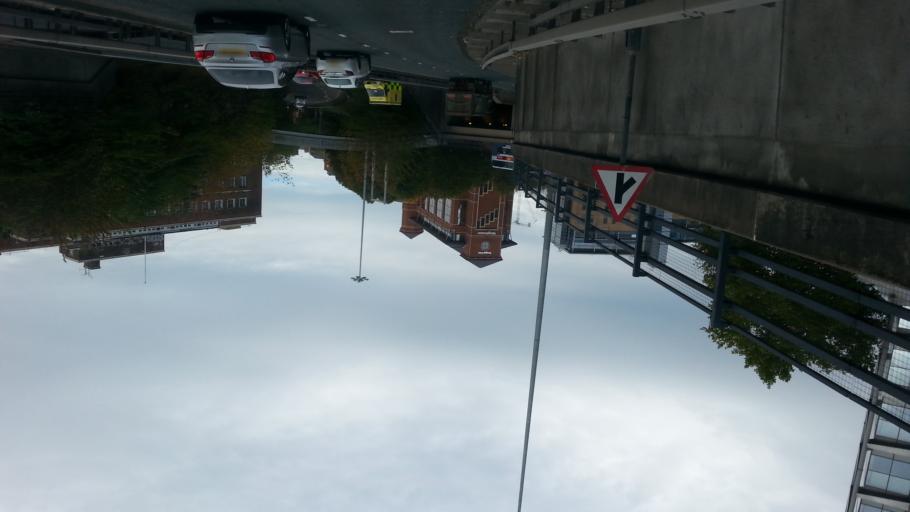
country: GB
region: England
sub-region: City and Borough of Leeds
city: Leeds
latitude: 53.7987
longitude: -1.5566
